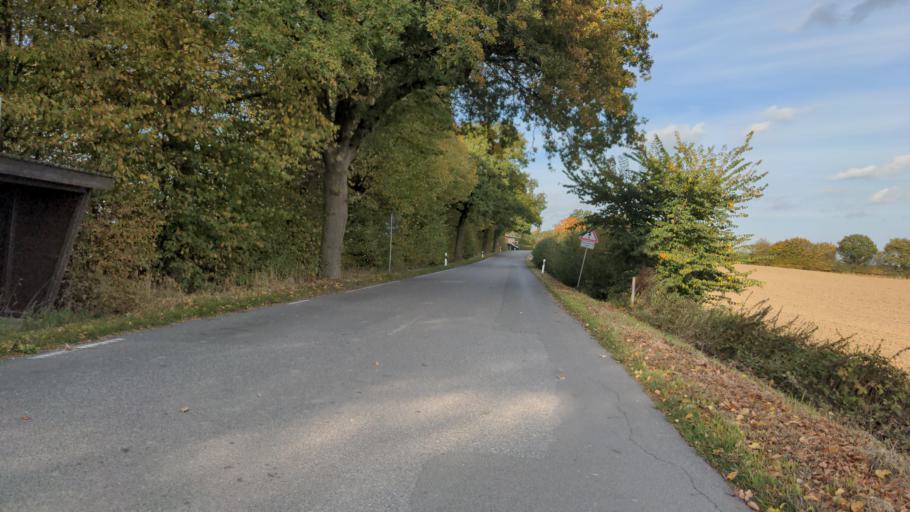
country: DE
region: Schleswig-Holstein
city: Ahrensbok
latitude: 53.9720
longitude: 10.5390
